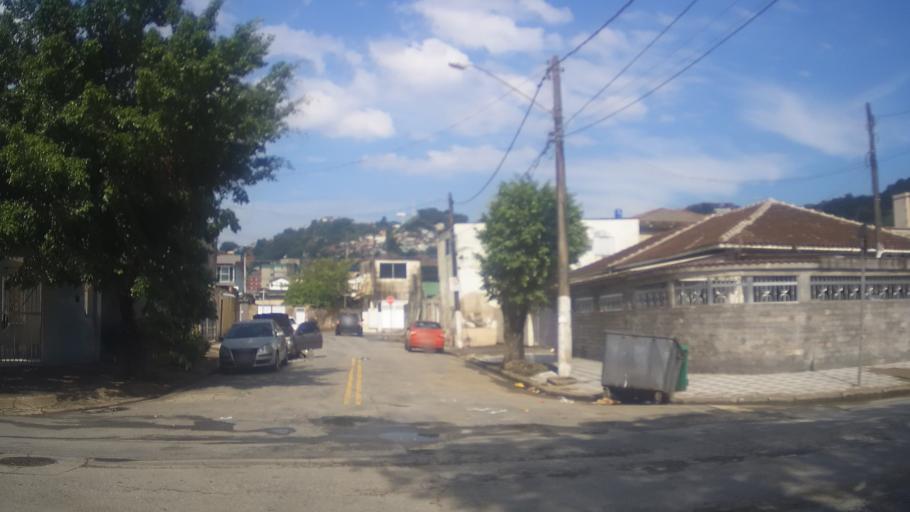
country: BR
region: Sao Paulo
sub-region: Santos
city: Santos
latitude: -23.9314
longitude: -46.3531
